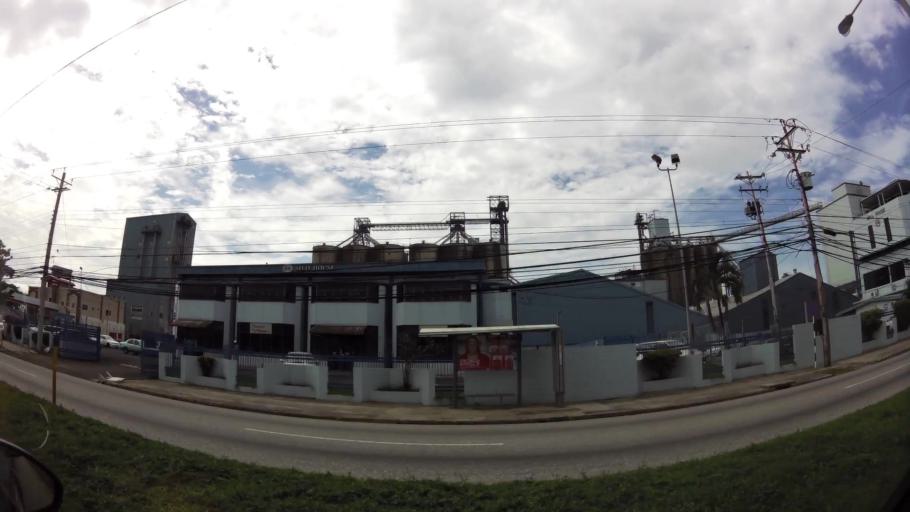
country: TT
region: City of Port of Spain
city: Port-of-Spain
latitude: 10.6595
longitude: -61.5244
